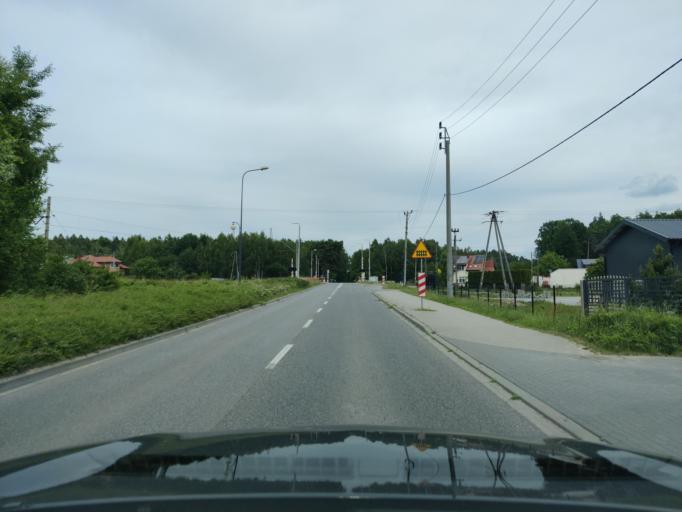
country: PL
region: Masovian Voivodeship
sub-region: Powiat wyszkowski
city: Wyszkow
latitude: 52.6198
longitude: 21.4524
